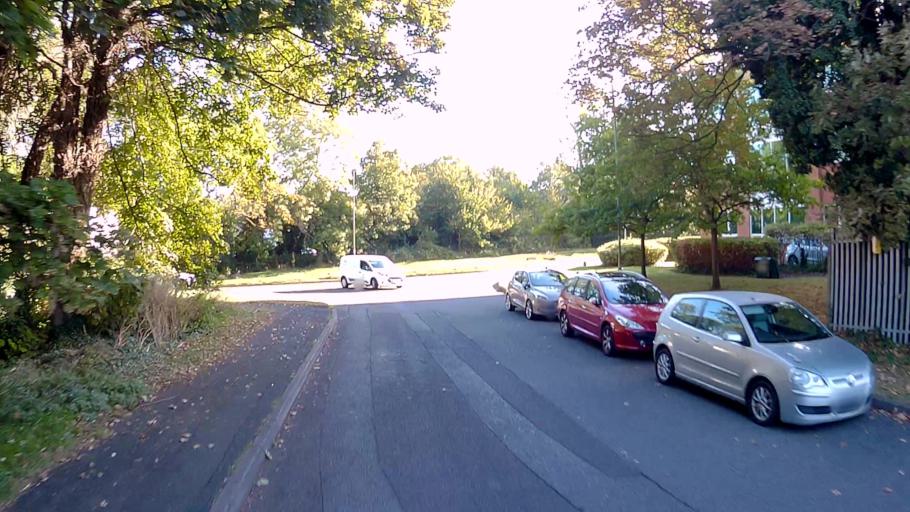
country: GB
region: England
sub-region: Hampshire
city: Basingstoke
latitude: 51.2469
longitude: -1.0982
